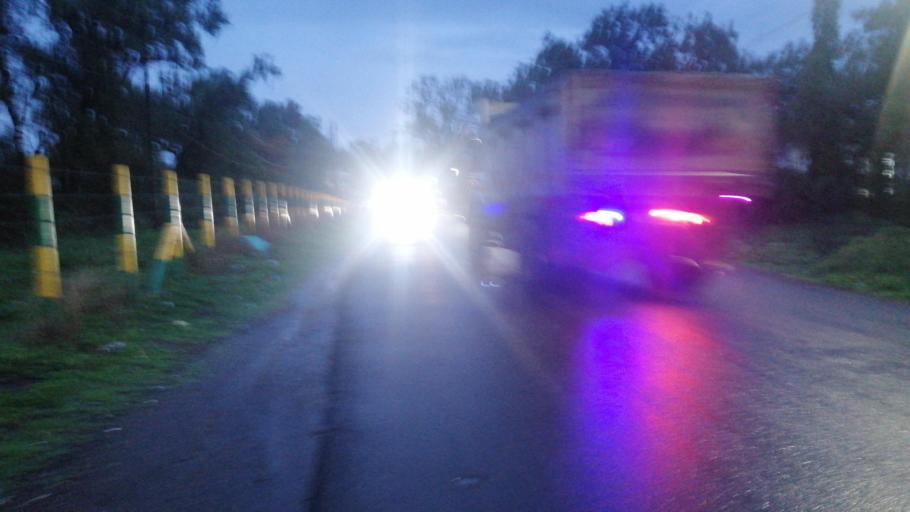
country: IN
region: Maharashtra
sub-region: Aurangabad Division
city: Aurangabad
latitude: 19.8774
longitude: 75.3769
